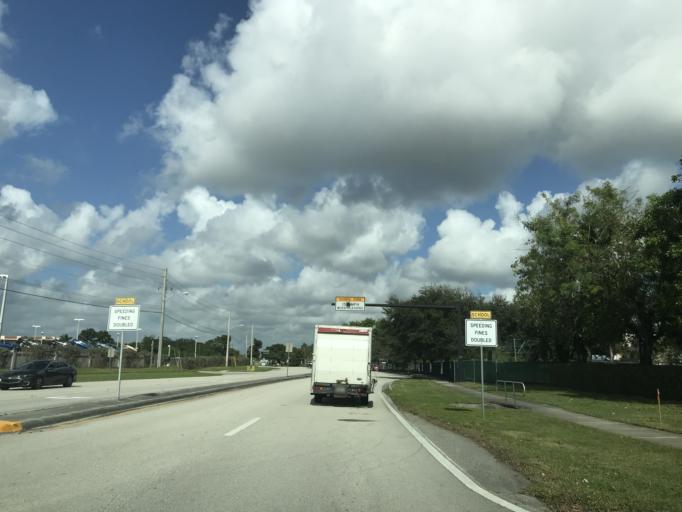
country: US
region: Florida
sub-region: Broward County
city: Coconut Creek
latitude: 26.2578
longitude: -80.1952
